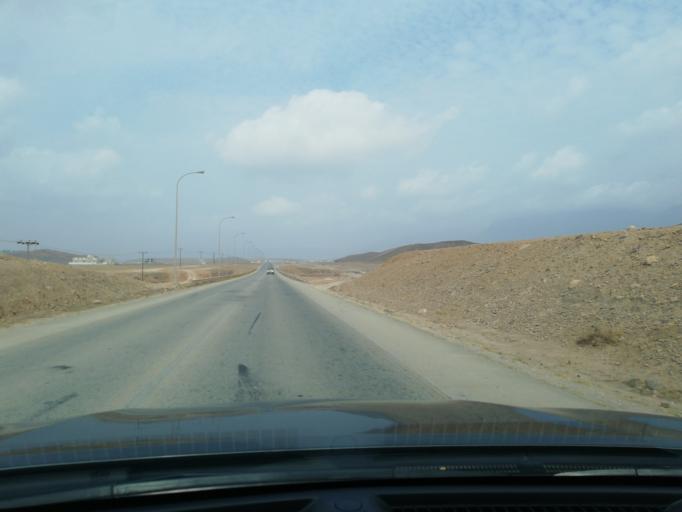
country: OM
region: Zufar
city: Salalah
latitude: 16.9611
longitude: 53.8832
